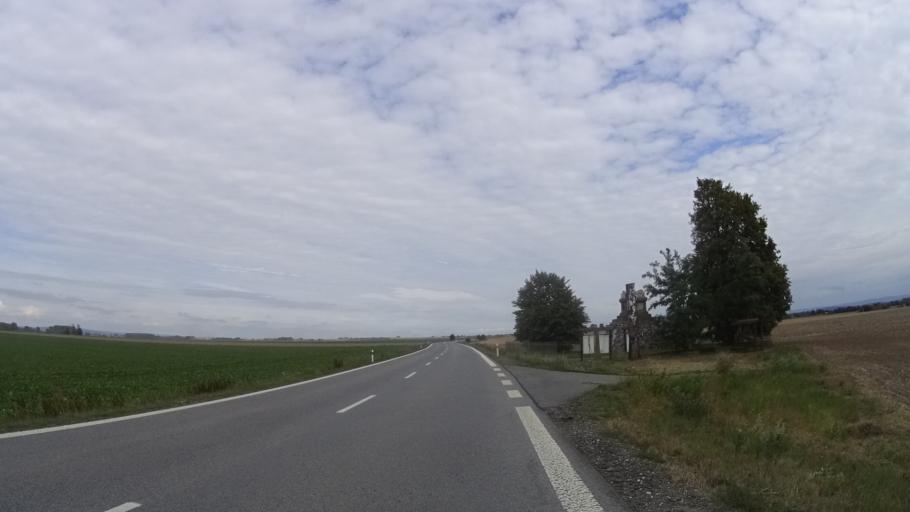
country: CZ
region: Olomoucky
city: Tovacov
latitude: 49.4456
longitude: 17.2797
